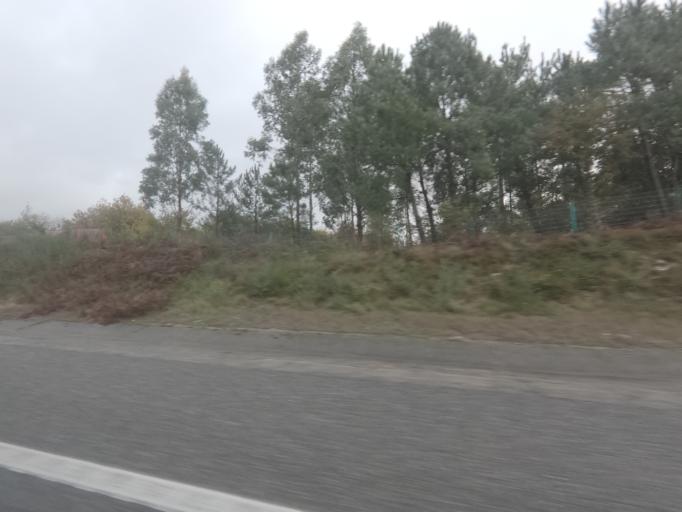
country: ES
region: Galicia
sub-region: Provincia de Pontevedra
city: Porrino
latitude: 42.1964
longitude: -8.6643
